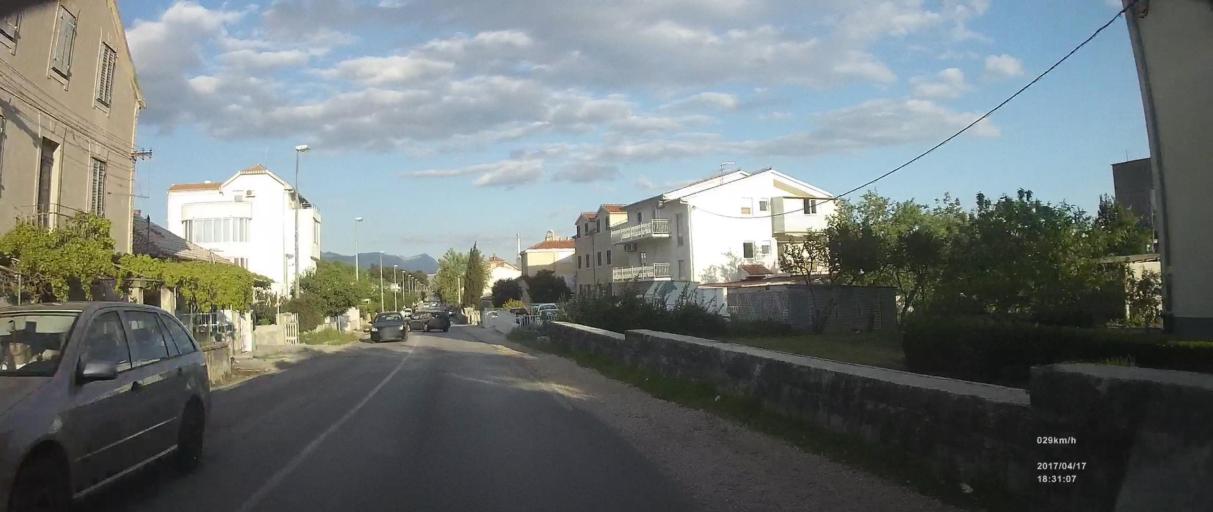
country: HR
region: Splitsko-Dalmatinska
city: Vranjic
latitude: 43.5456
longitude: 16.4317
